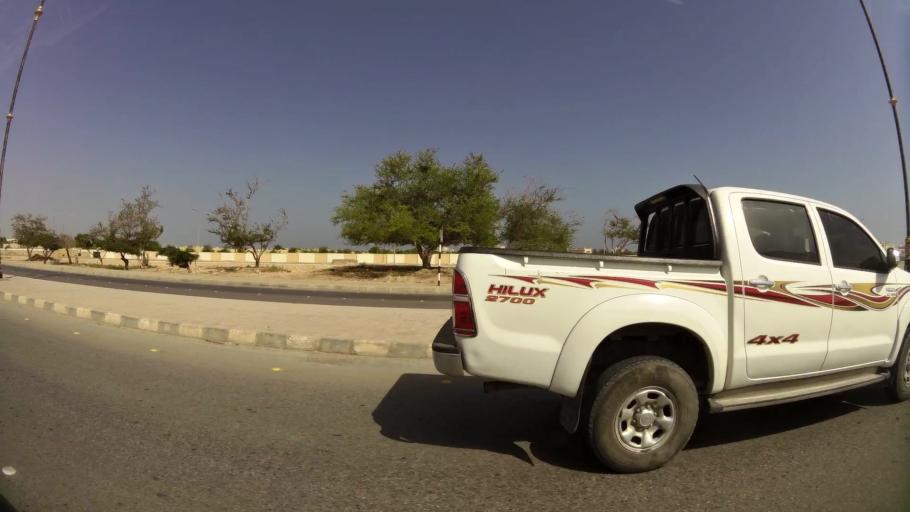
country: OM
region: Zufar
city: Salalah
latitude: 17.0100
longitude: 54.0445
